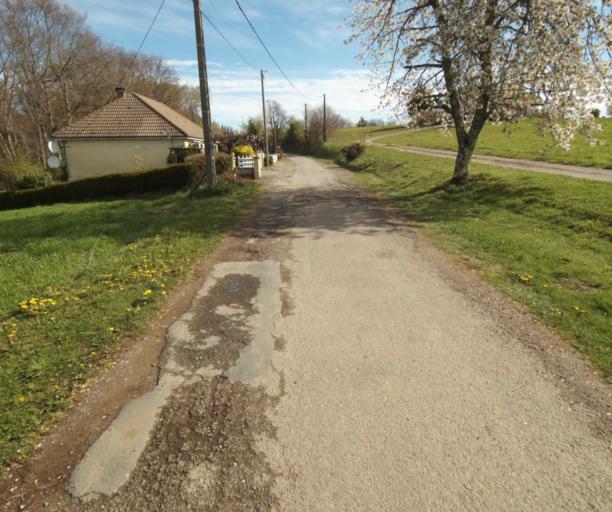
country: FR
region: Limousin
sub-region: Departement de la Correze
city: Laguenne
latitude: 45.2792
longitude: 1.8287
